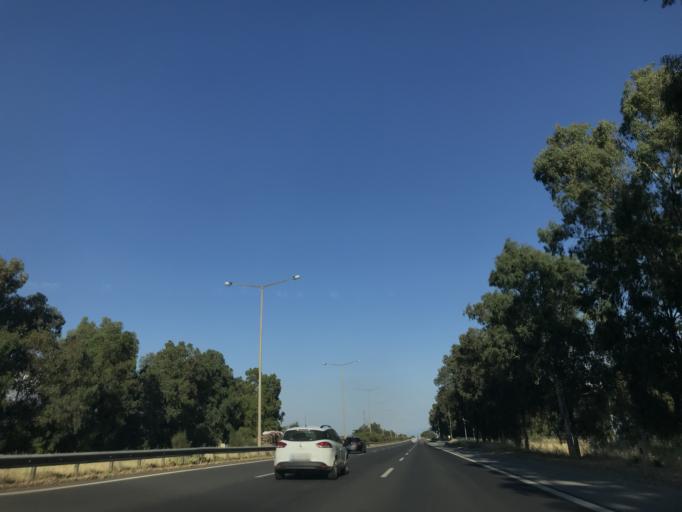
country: TR
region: Aydin
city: Germencik
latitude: 37.8756
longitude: 27.6143
